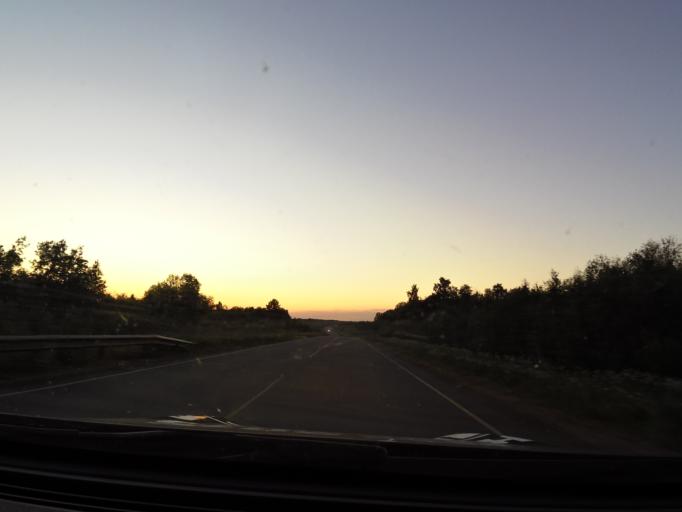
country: RU
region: Vologda
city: Vytegra
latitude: 60.9499
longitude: 36.0908
